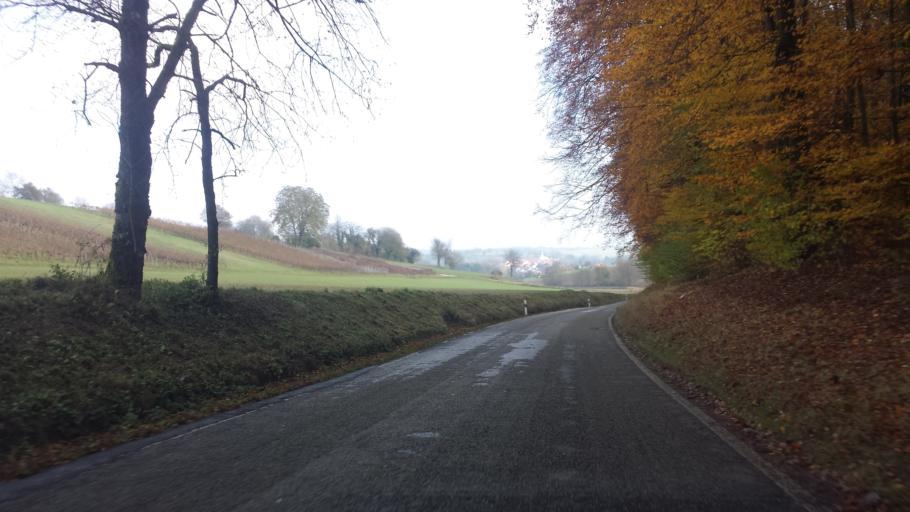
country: DE
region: Baden-Wuerttemberg
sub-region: Karlsruhe Region
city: Bretten
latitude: 49.1005
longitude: 8.7231
